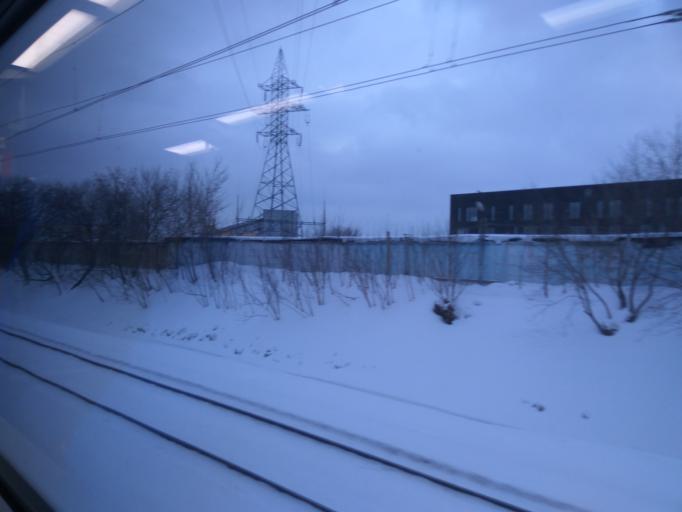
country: RU
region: Moscow
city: Sokol
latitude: 55.7760
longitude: 37.5081
